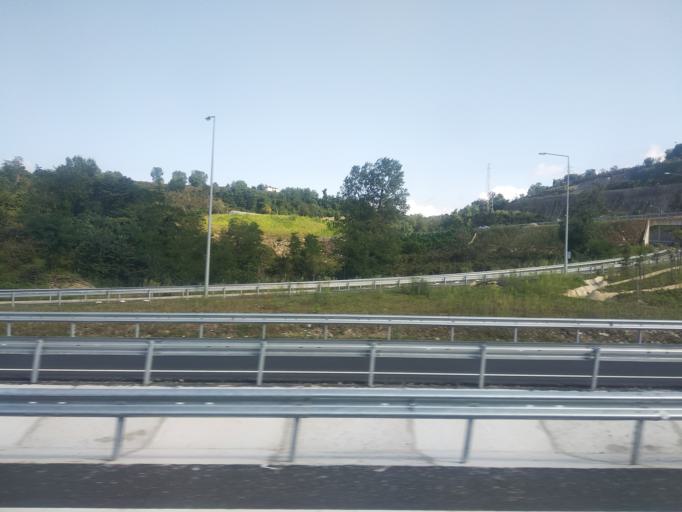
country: TR
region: Ordu
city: Ordu
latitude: 40.9904
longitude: 37.8137
